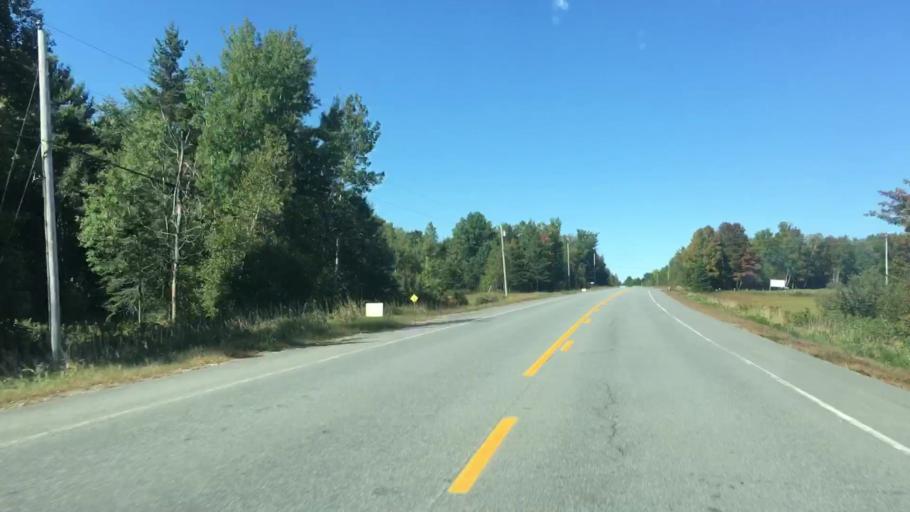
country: US
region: Maine
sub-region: Piscataquis County
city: Sangerville
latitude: 45.0701
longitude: -69.4589
